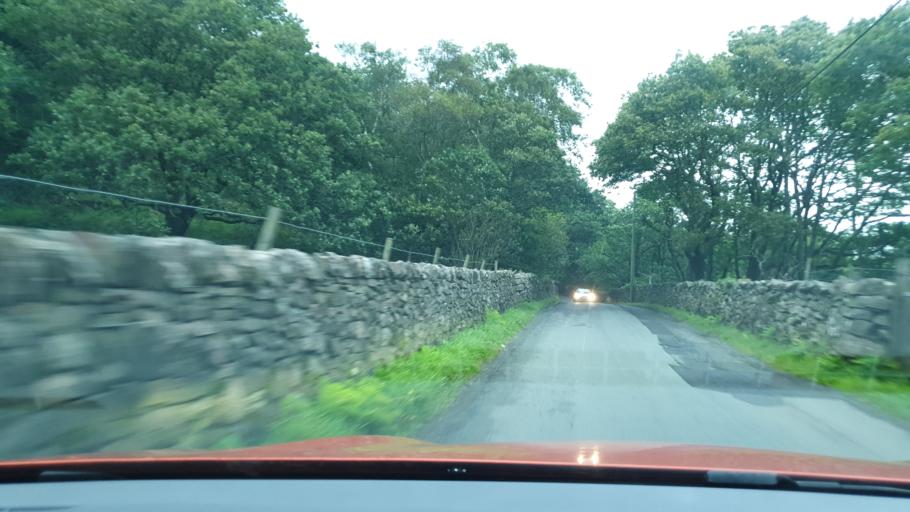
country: GB
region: England
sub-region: Cumbria
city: Millom
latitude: 54.3904
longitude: -3.2922
